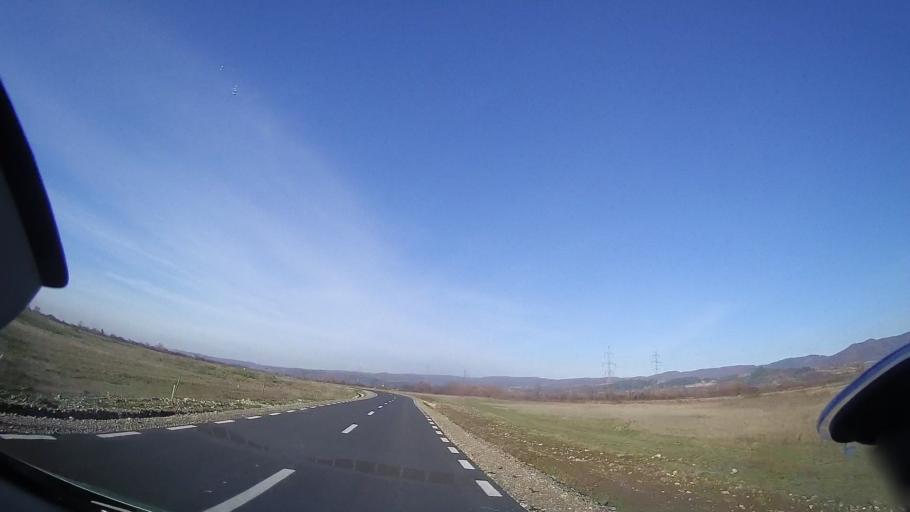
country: RO
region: Bihor
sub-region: Comuna Auseu
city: Auseu
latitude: 47.0101
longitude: 22.5016
